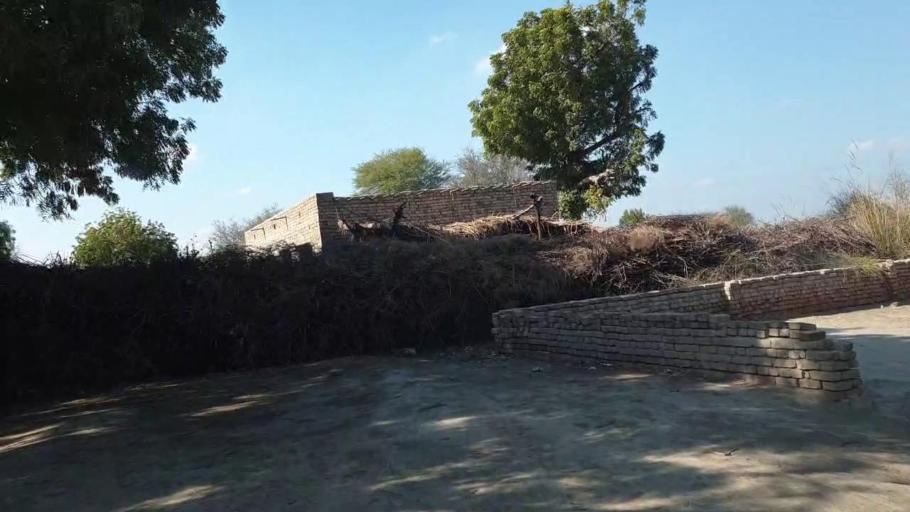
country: PK
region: Sindh
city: Shahpur Chakar
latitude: 26.0892
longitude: 68.5831
